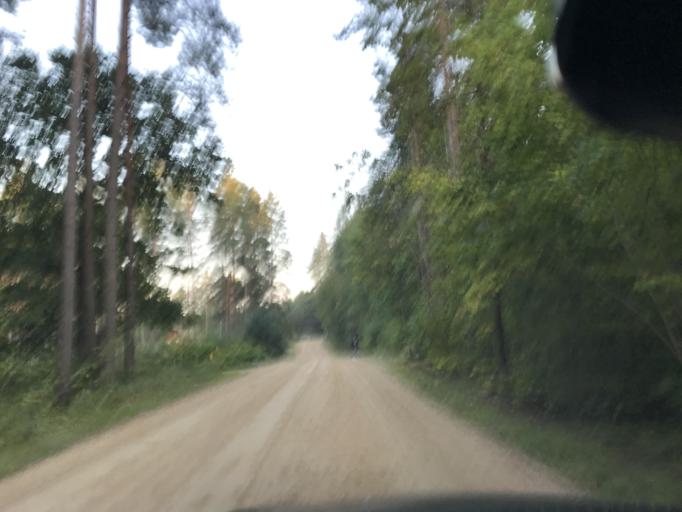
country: LV
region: Ikskile
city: Ikskile
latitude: 56.8305
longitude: 24.5101
